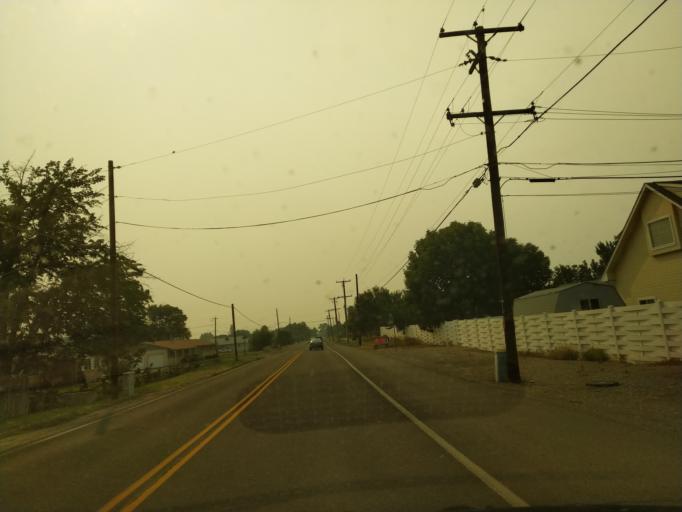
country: US
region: Colorado
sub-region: Mesa County
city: Fruitvale
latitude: 39.0846
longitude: -108.4917
